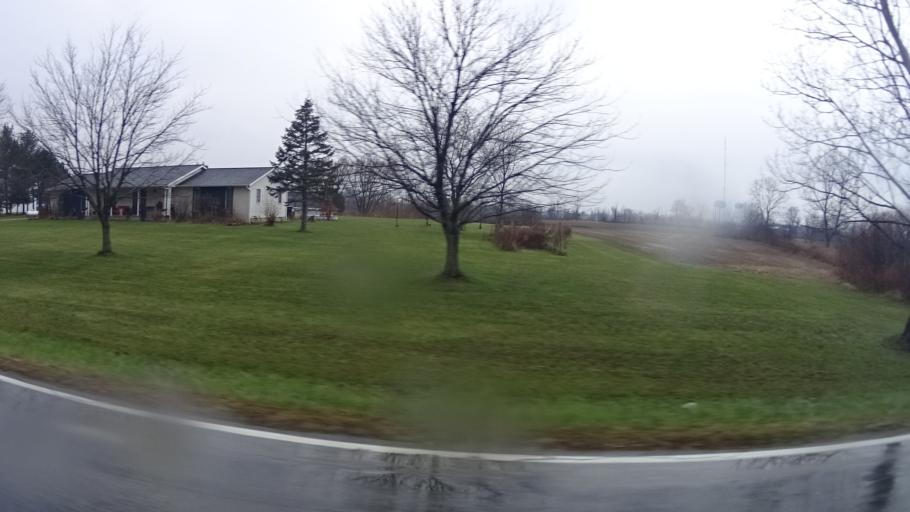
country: US
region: Ohio
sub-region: Lorain County
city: Lagrange
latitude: 41.2320
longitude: -82.1392
